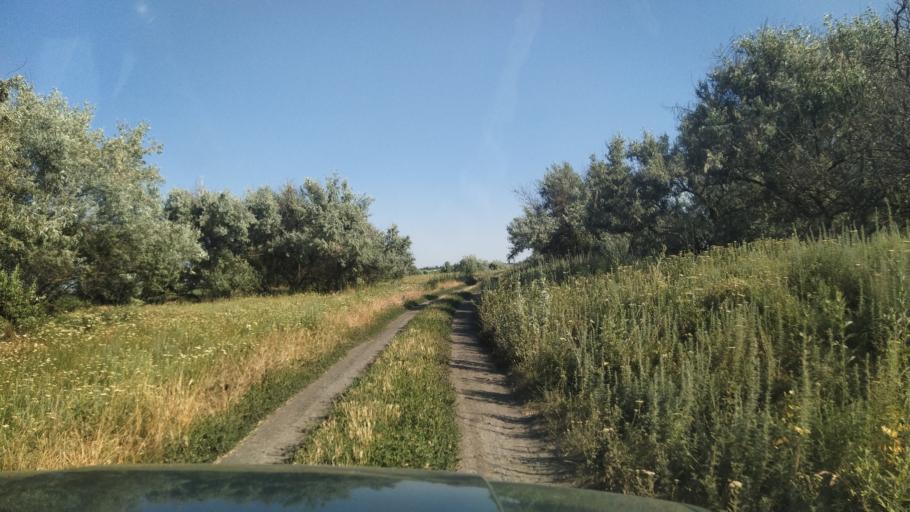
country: RU
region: Rostov
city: Kuleshovka
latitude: 47.1338
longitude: 39.6419
